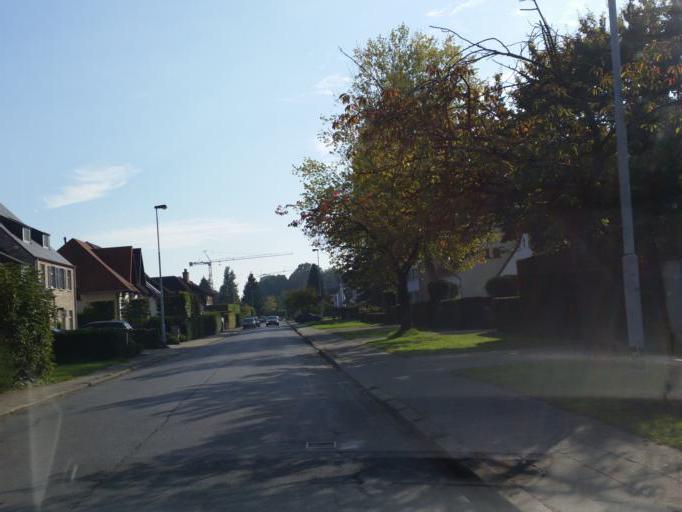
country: BE
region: Flanders
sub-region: Provincie Antwerpen
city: Hove
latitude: 51.1610
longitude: 4.4709
